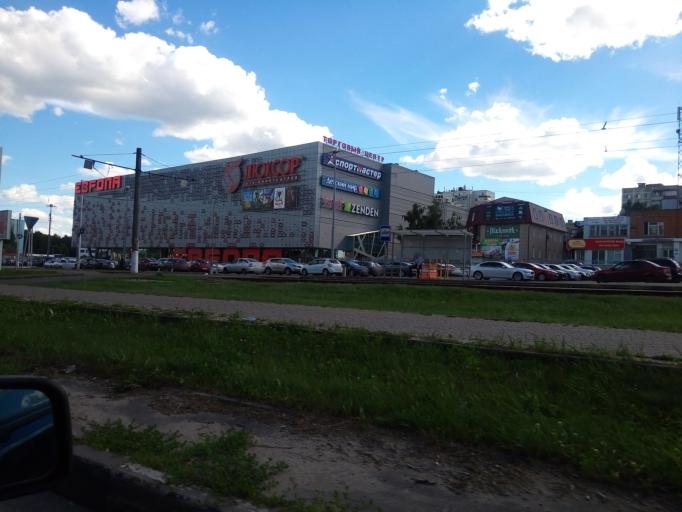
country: RU
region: Kursk
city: Kursk
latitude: 51.7429
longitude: 36.1465
